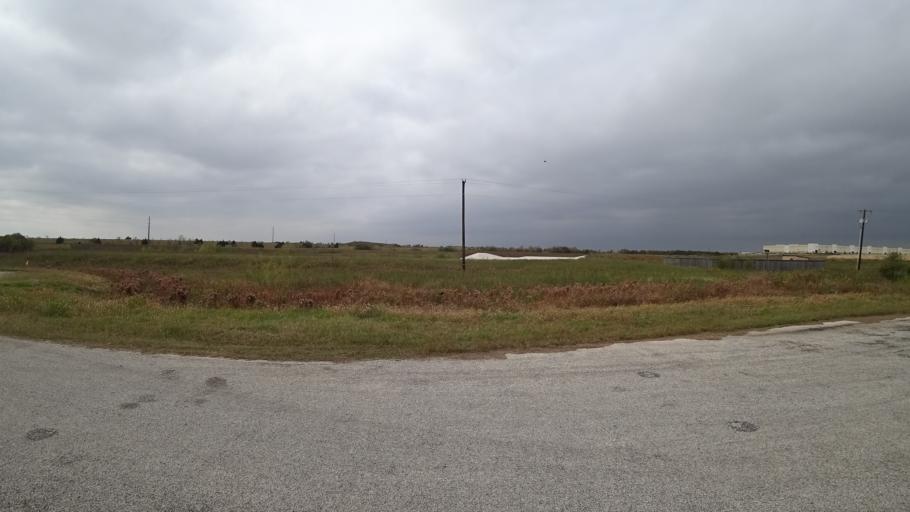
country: US
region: Texas
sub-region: Travis County
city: Pflugerville
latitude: 30.4130
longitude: -97.5861
